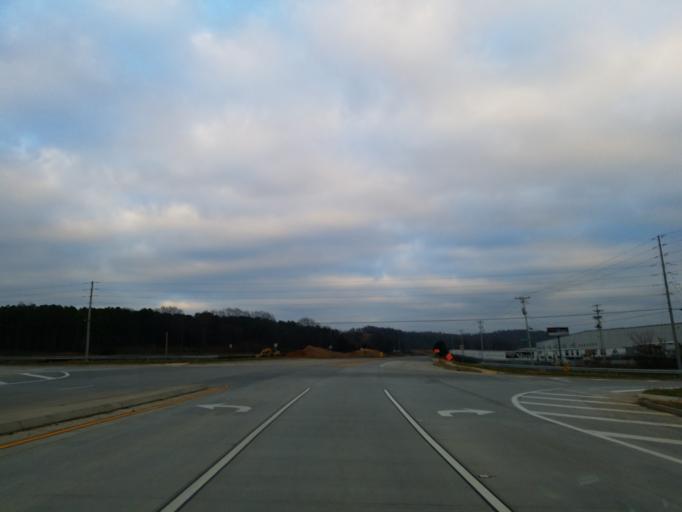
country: US
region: Georgia
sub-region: Gordon County
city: Calhoun
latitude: 34.4421
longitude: -84.9150
